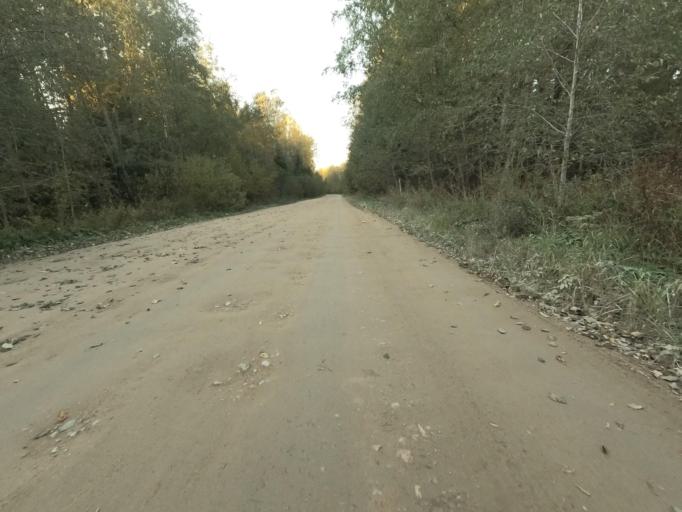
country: RU
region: Leningrad
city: Lyuban'
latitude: 59.0121
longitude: 31.0891
